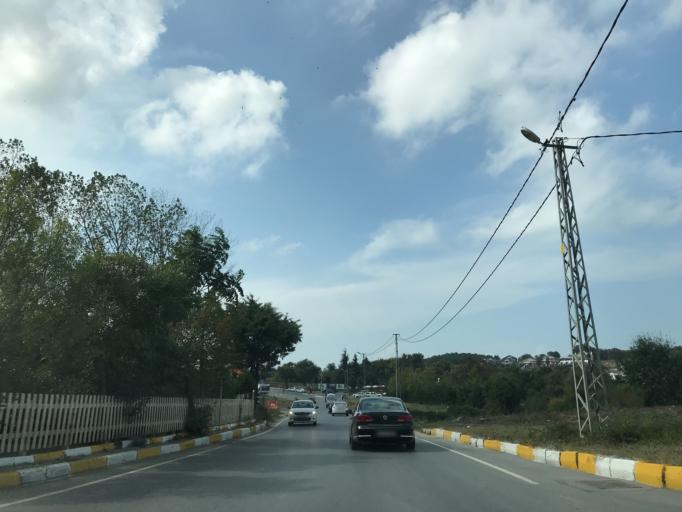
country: TR
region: Istanbul
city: Arikoey
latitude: 41.2187
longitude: 29.0346
